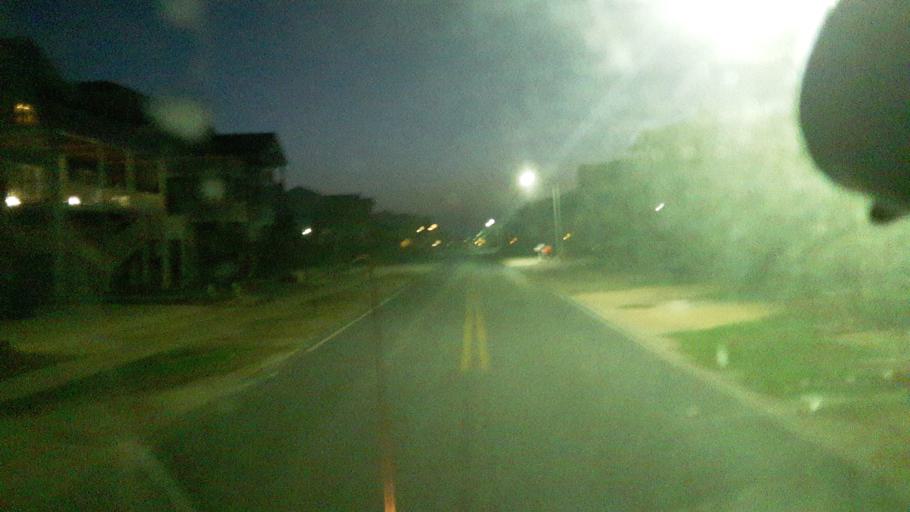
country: US
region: North Carolina
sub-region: Brunswick County
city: Shallotte
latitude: 33.8925
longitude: -78.4175
